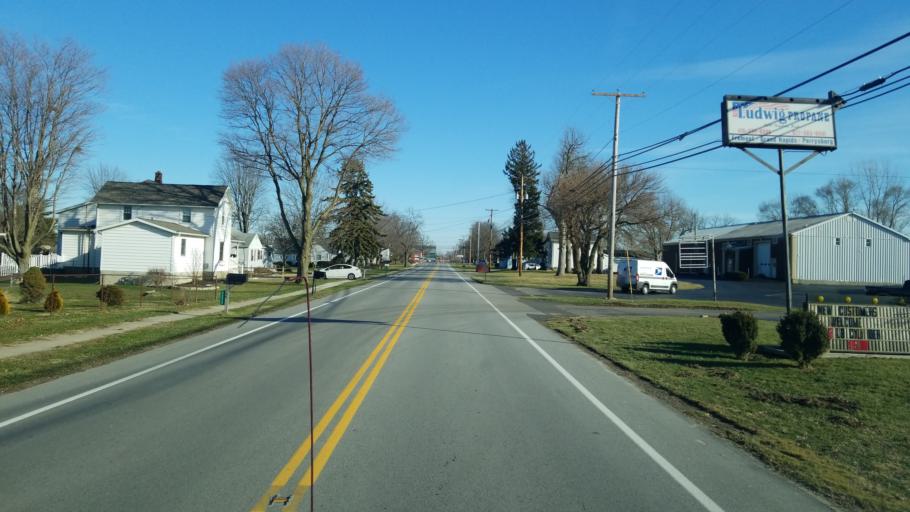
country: US
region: Ohio
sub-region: Sandusky County
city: Stony Prairie
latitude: 41.3494
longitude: -83.1440
